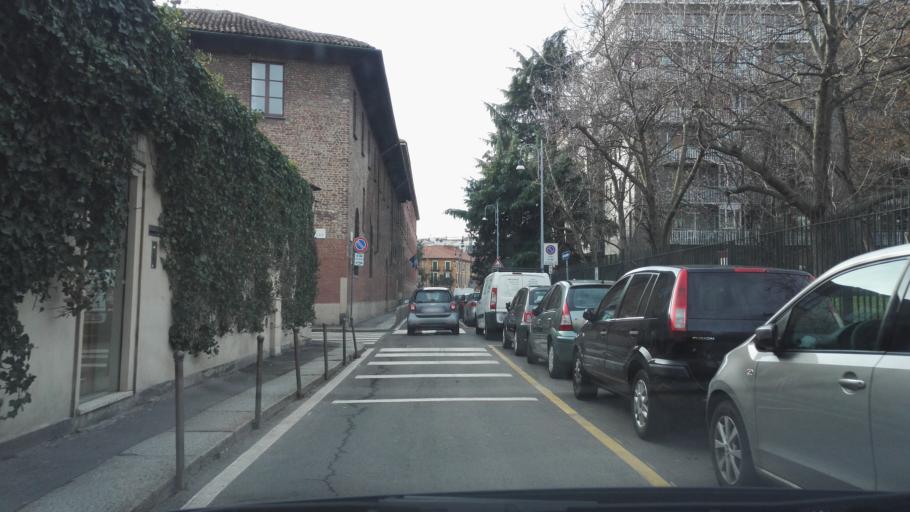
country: IT
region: Lombardy
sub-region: Citta metropolitana di Milano
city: Milano
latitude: 45.4566
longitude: 9.1798
